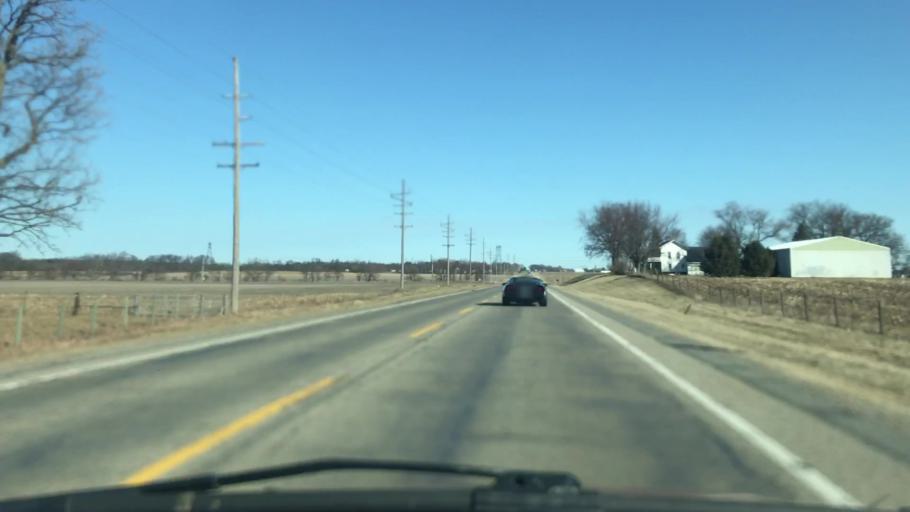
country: US
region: Indiana
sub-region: Porter County
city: Kouts
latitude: 41.3595
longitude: -87.0270
